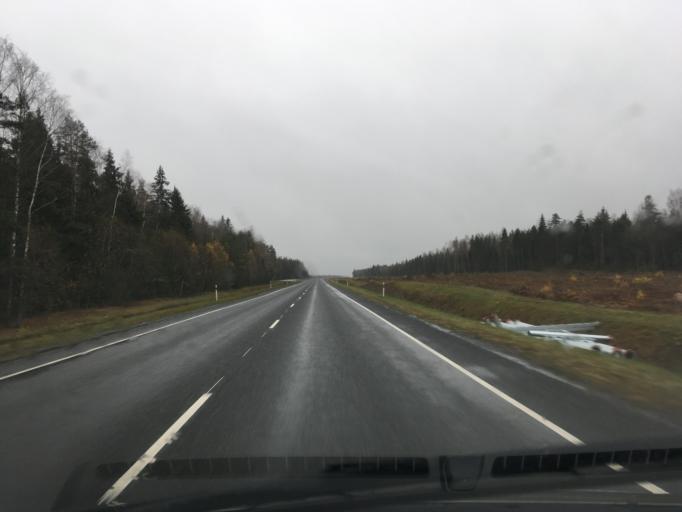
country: EE
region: Harju
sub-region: Nissi vald
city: Turba
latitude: 58.9632
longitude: 24.0715
